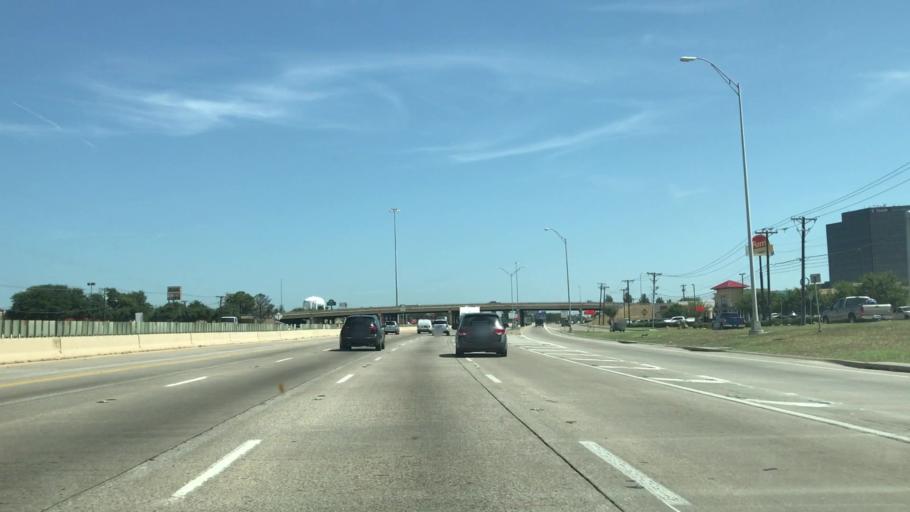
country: US
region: Texas
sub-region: Collin County
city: Plano
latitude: 33.0257
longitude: -96.7097
